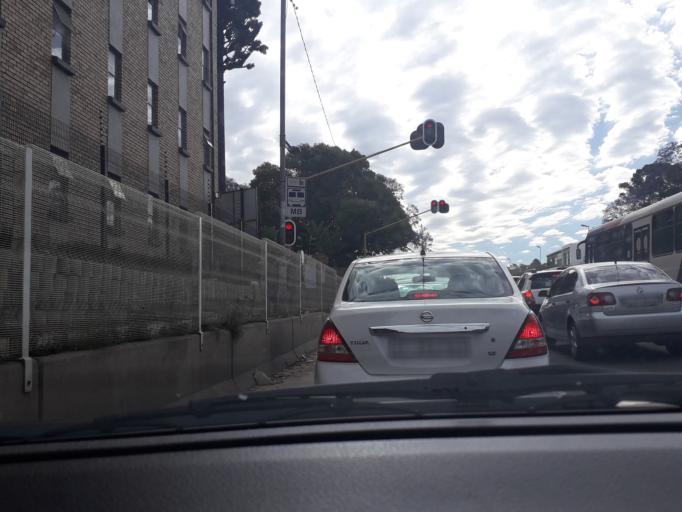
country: ZA
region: Gauteng
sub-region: City of Johannesburg Metropolitan Municipality
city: Johannesburg
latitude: -26.1837
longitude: 28.0066
